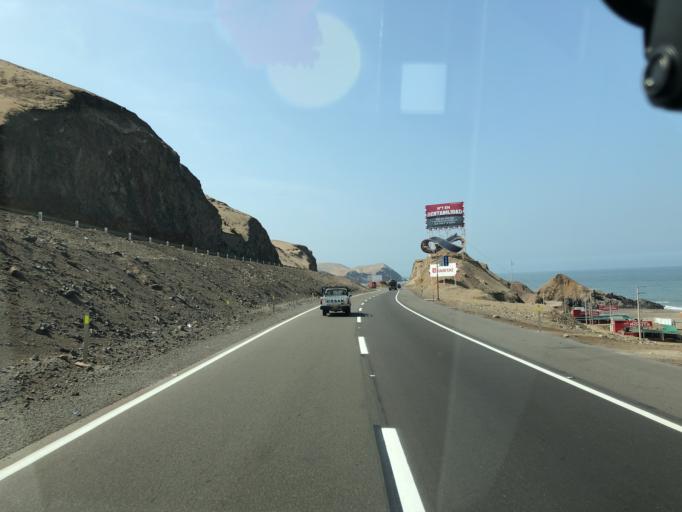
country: PE
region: Lima
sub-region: Provincia de Canete
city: Mala
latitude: -12.6312
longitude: -76.6695
